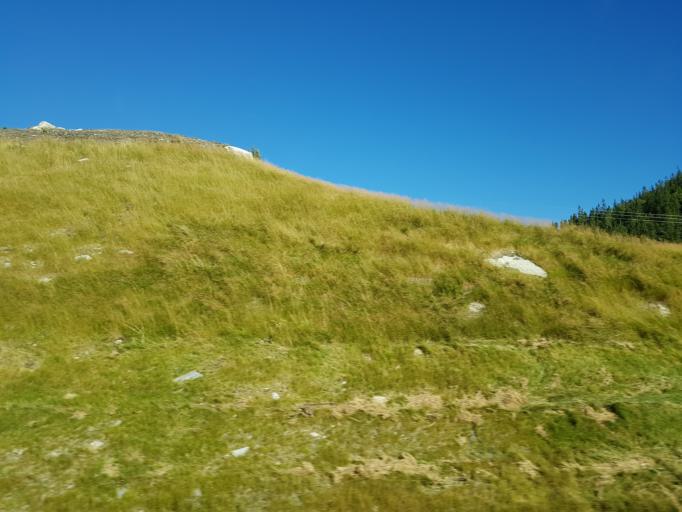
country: NO
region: Sor-Trondelag
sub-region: Afjord
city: A i Afjord
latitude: 63.6969
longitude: 10.2422
